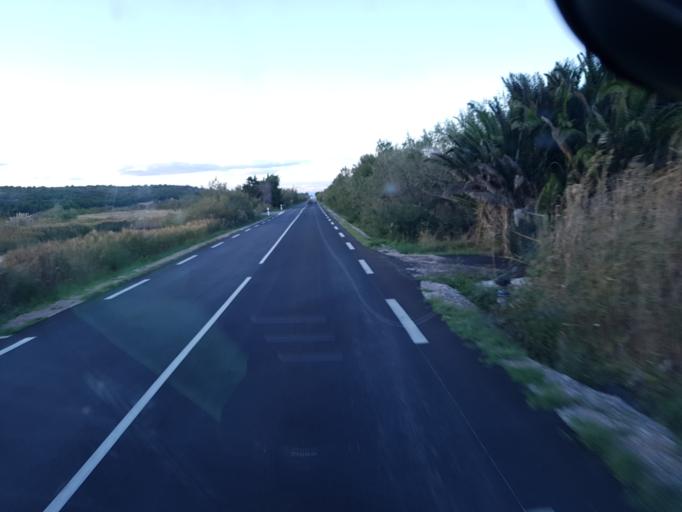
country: FR
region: Languedoc-Roussillon
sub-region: Departement de l'Aude
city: Port-la-Nouvelle
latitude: 42.9978
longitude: 3.0420
